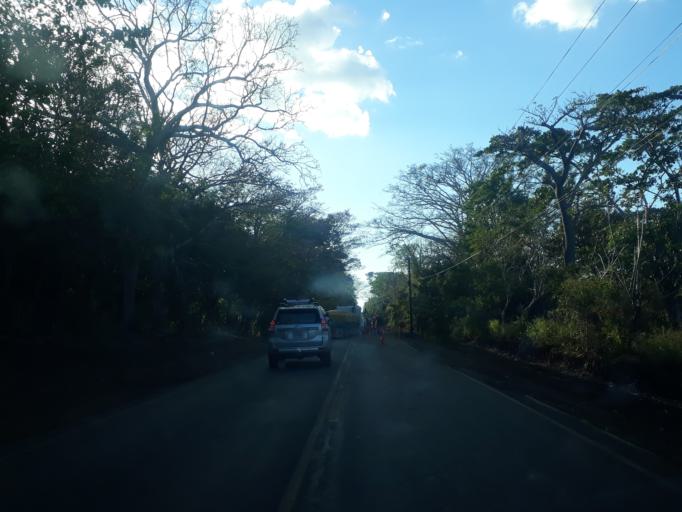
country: NI
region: Carazo
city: La Paz de Oriente
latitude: 11.8090
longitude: -86.1197
